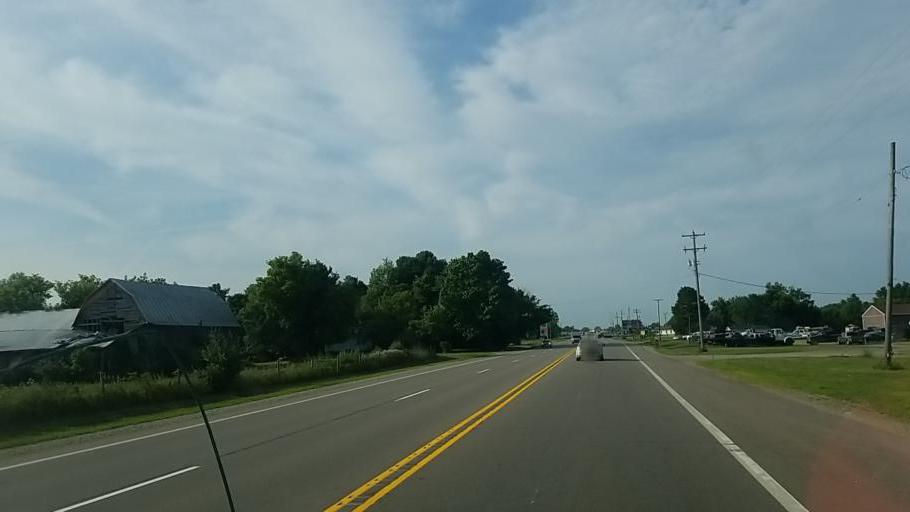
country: US
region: Michigan
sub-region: Ionia County
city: Ionia
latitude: 42.8895
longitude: -85.0750
